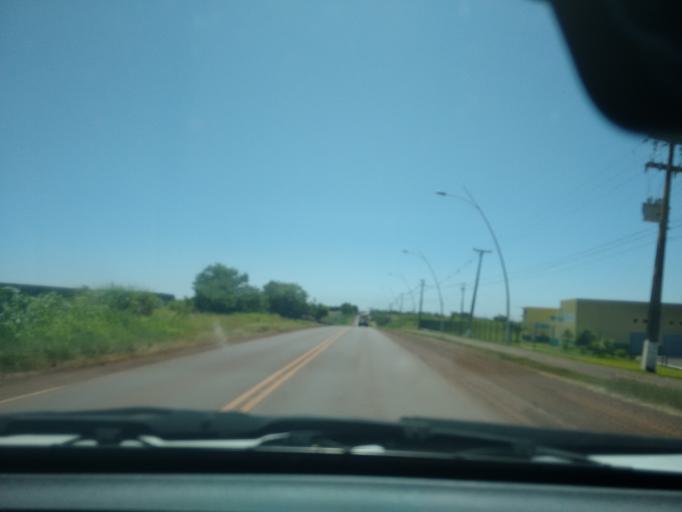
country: BR
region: Parana
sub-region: Marechal Candido Rondon
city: Marechal Candido Rondon
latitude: -24.5575
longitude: -54.1030
